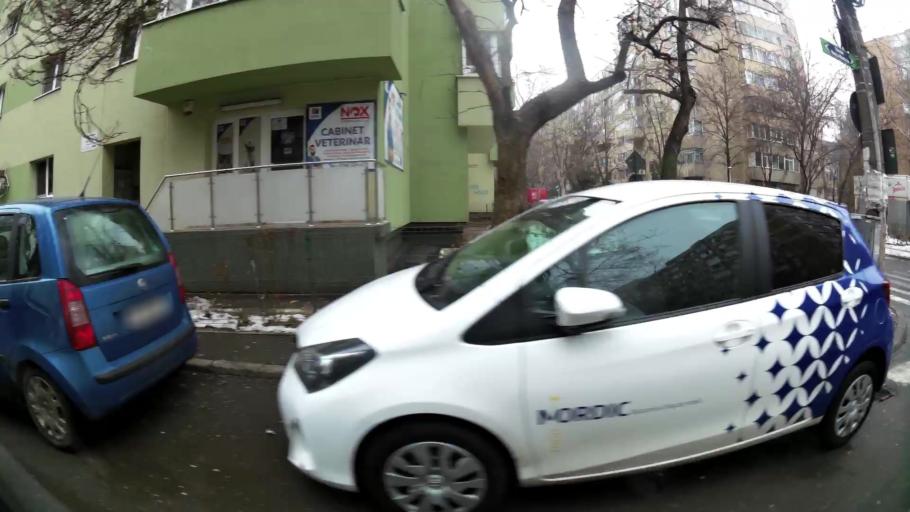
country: RO
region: Ilfov
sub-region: Comuna Chiajna
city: Rosu
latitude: 44.4361
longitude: 26.0263
